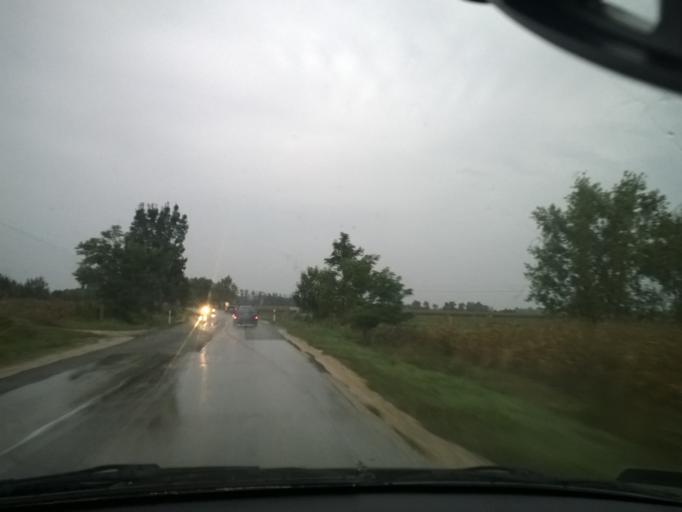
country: HU
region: Pest
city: Kiskunlachaza
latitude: 47.1535
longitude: 18.9991
